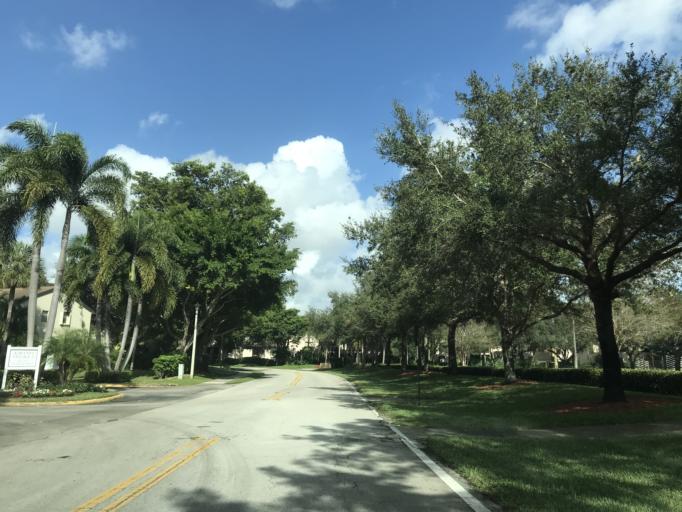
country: US
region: Florida
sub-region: Broward County
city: Coconut Creek
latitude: 26.2659
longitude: -80.1893
